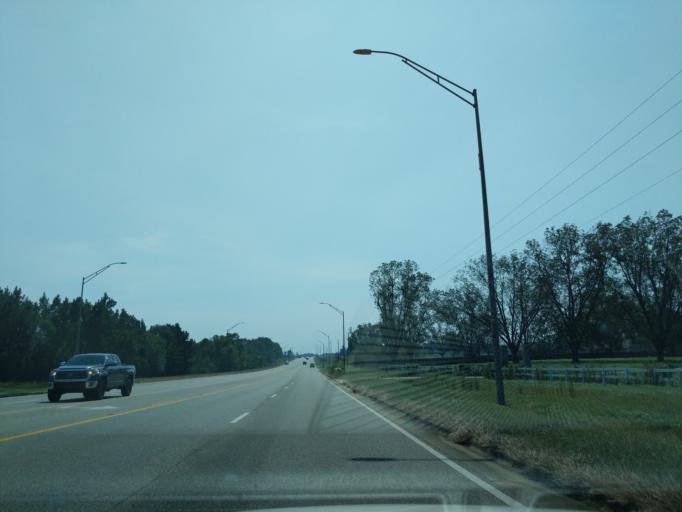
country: US
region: Alabama
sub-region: Covington County
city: Andalusia
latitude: 31.2839
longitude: -86.5048
